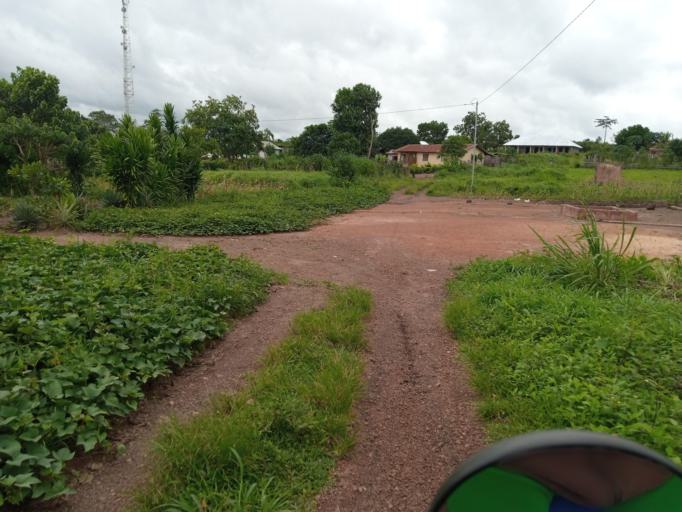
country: SL
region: Southern Province
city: Largo
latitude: 8.1936
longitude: -12.0560
